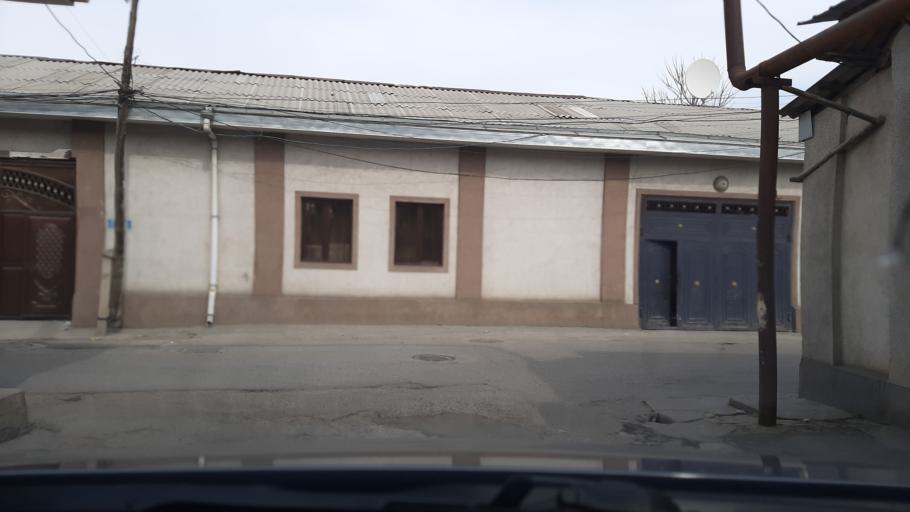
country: TJ
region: Dushanbe
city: Dushanbe
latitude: 38.5635
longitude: 68.7742
